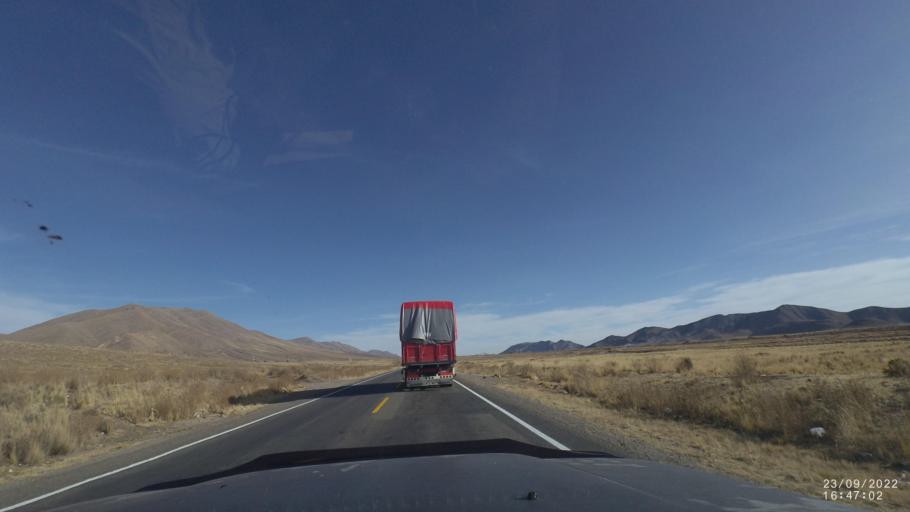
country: BO
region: Oruro
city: Poopo
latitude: -18.3634
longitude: -66.9821
